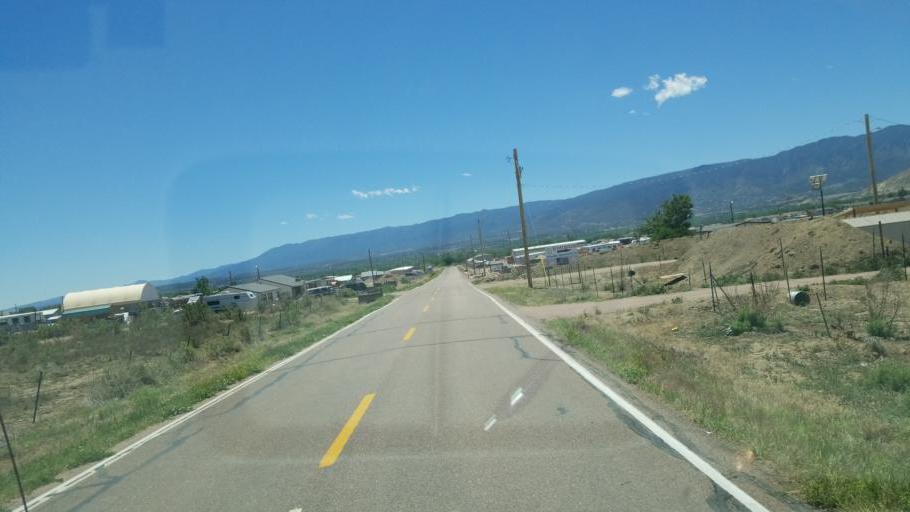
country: US
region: Colorado
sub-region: Fremont County
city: Canon City
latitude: 38.4765
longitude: -105.2226
